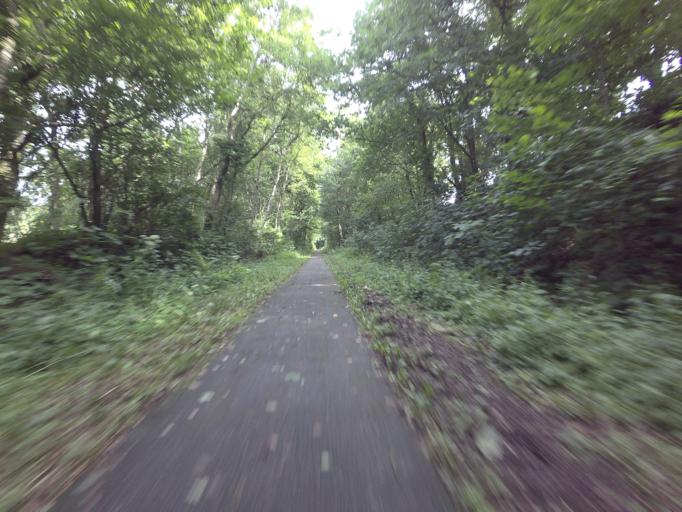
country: DK
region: Central Jutland
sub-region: Favrskov Kommune
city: Hammel
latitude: 56.3157
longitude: 9.8652
